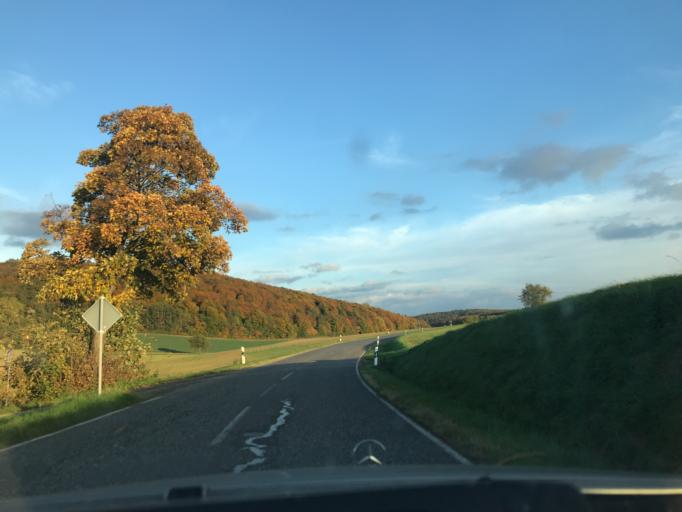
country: DE
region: Hesse
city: Witzenhausen
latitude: 51.4086
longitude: 9.8560
